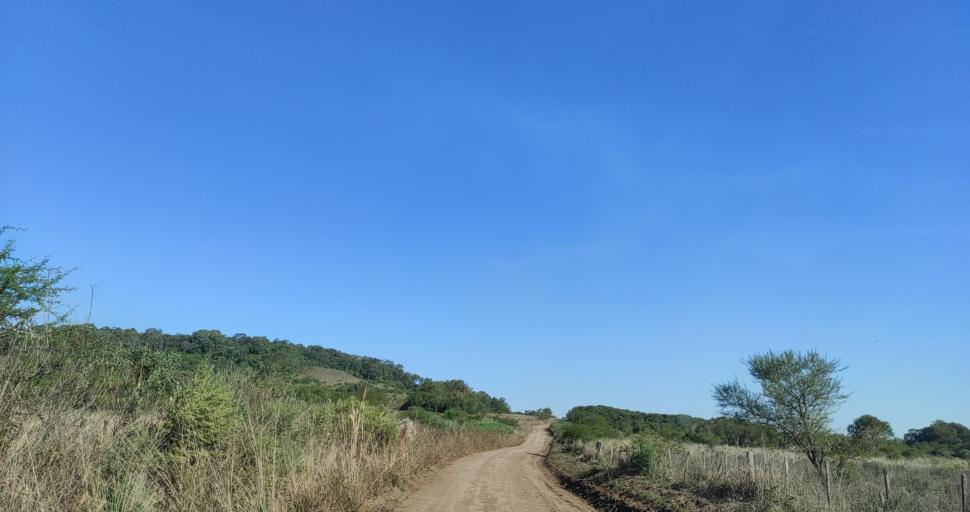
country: AR
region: Misiones
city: Cerro Cora
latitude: -27.6650
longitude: -55.6598
